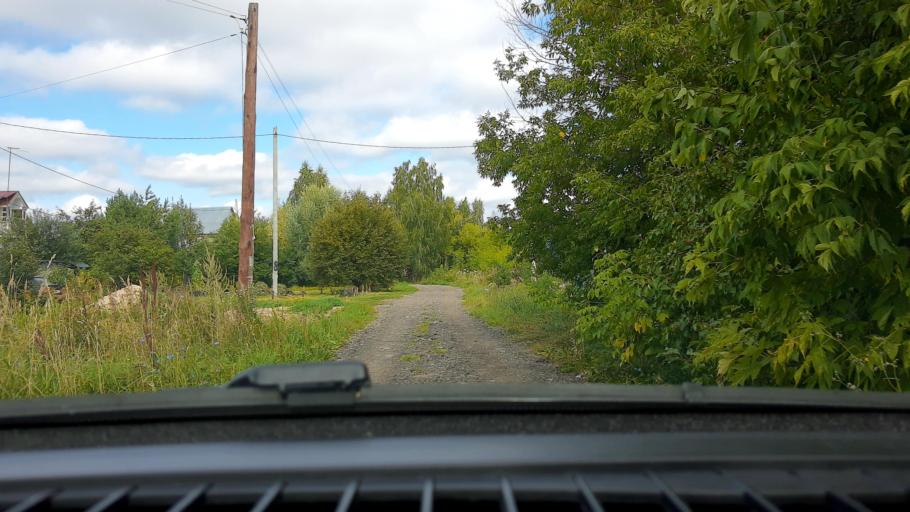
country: RU
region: Nizjnij Novgorod
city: Gorbatovka
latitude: 56.2674
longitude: 43.7763
